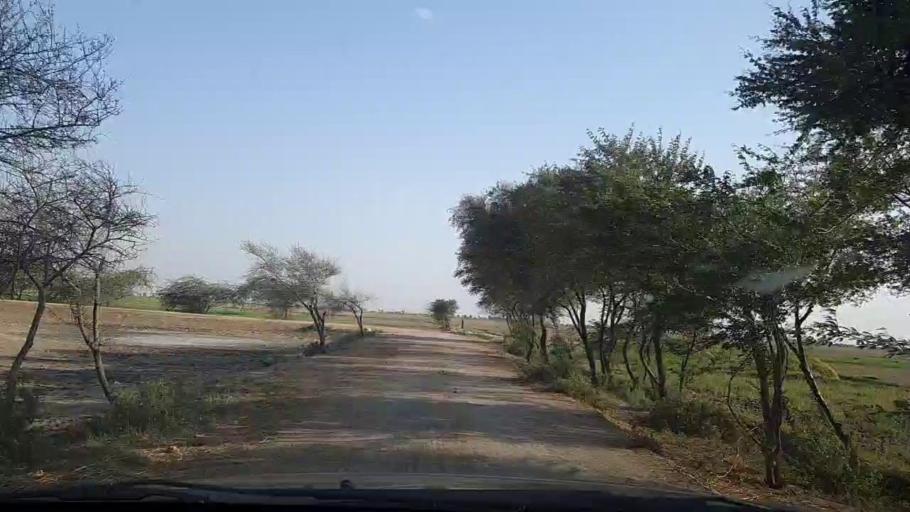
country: PK
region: Sindh
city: Chuhar Jamali
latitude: 24.5483
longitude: 68.1066
